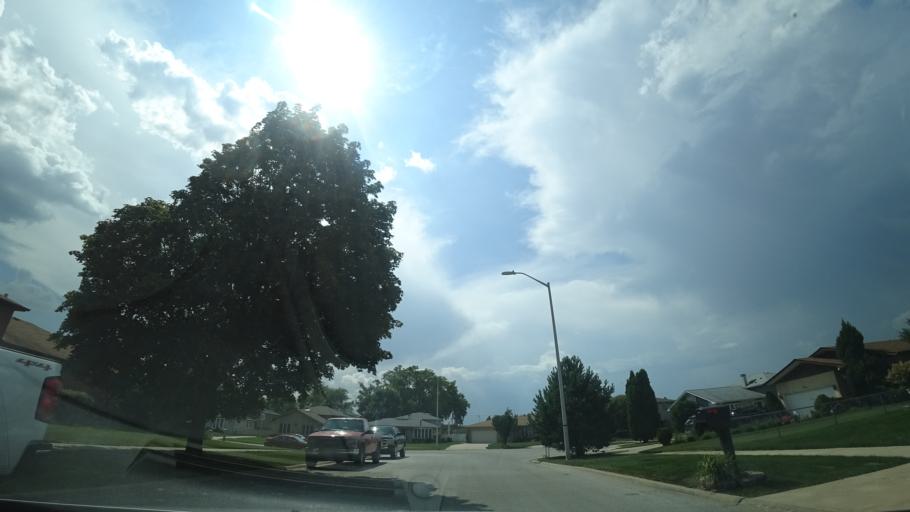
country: US
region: Illinois
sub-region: Cook County
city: Merrionette Park
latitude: 41.6725
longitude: -87.7173
